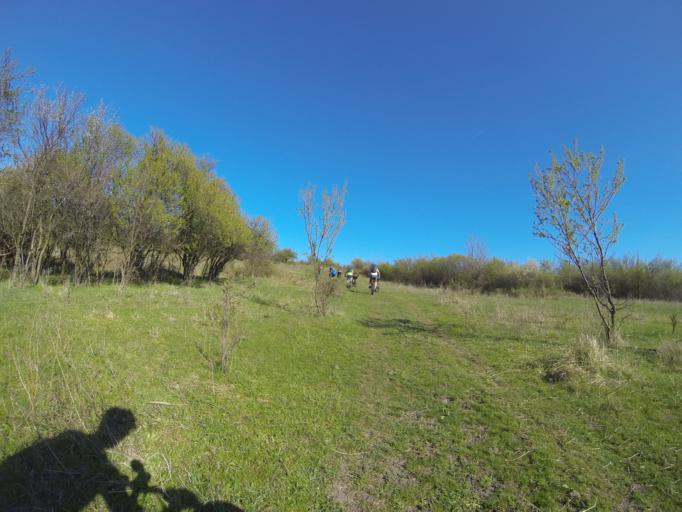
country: RO
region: Dolj
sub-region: Comuna Goesti
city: Goesti
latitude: 44.5049
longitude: 23.8003
